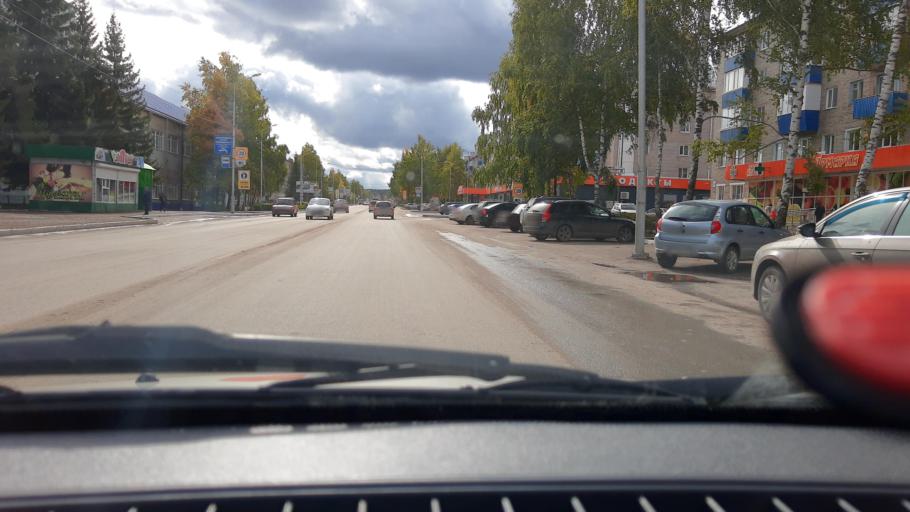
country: RU
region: Bashkortostan
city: Belebey
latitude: 54.1020
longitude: 54.1092
